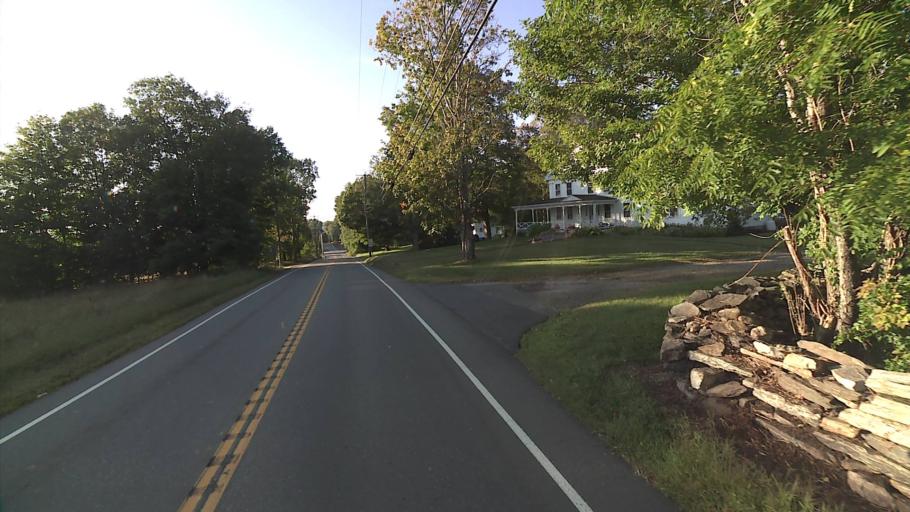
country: US
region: Connecticut
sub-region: Tolland County
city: South Coventry
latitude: 41.8061
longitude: -72.3044
